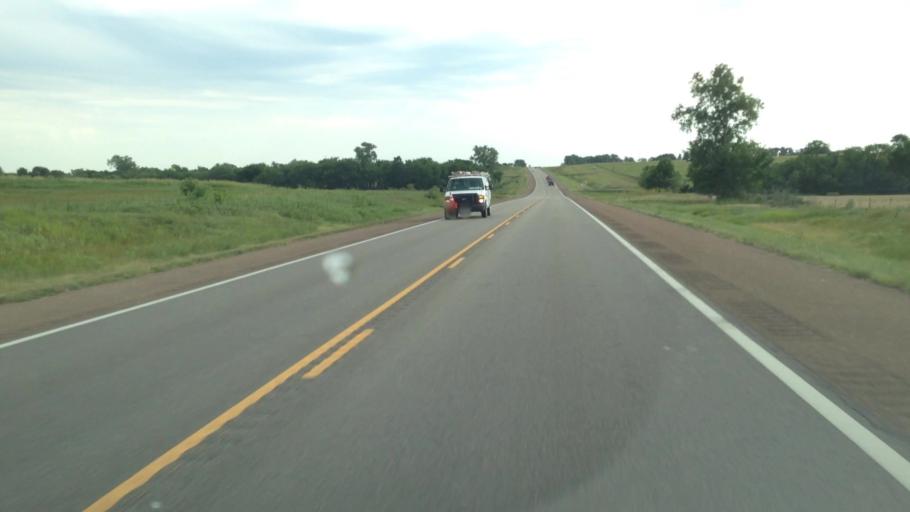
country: US
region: Kansas
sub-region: Woodson County
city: Yates Center
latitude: 38.0154
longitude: -95.7392
